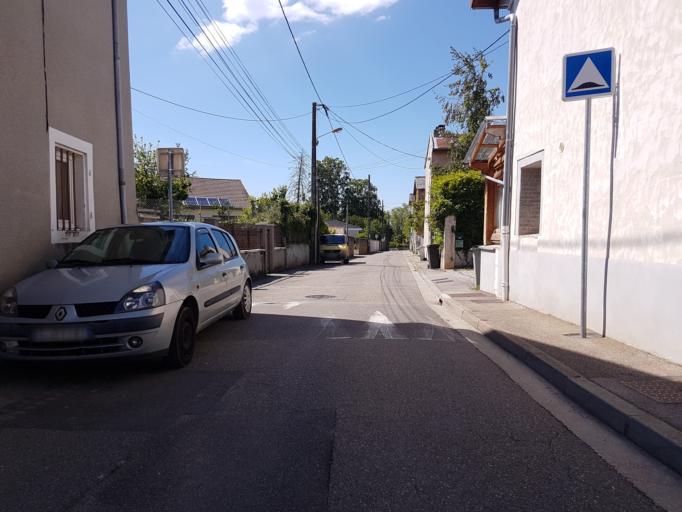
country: FR
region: Rhone-Alpes
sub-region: Departement du Rhone
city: Jonage
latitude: 45.7968
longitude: 5.0433
